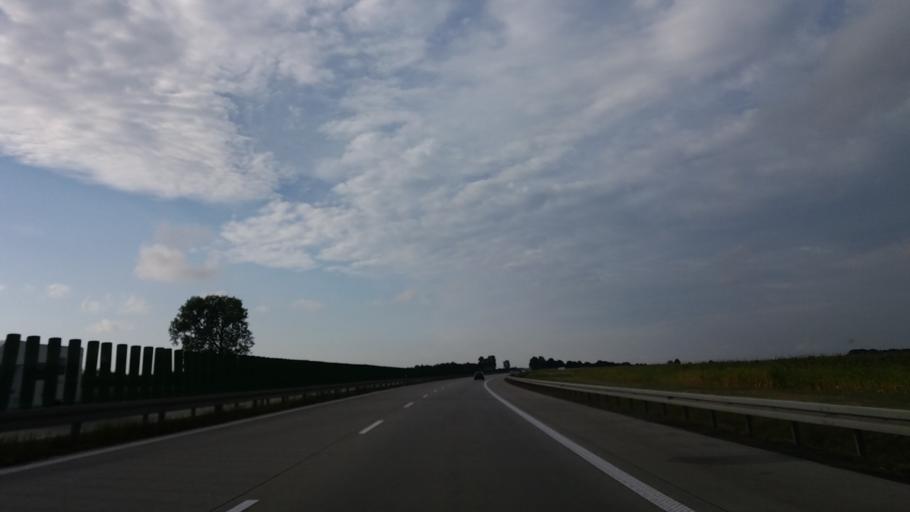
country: PL
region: Lower Silesian Voivodeship
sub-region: Powiat sredzki
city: Udanin
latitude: 51.0942
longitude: 16.4088
